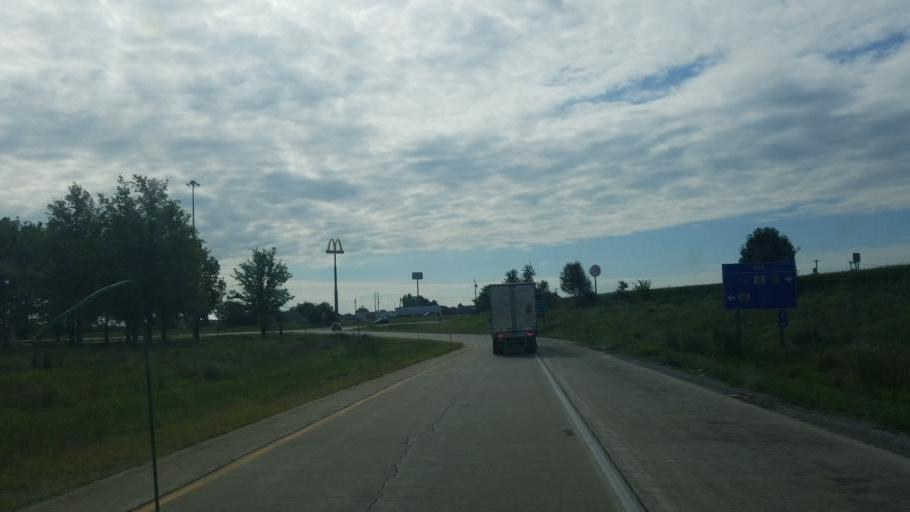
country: US
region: Illinois
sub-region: Clark County
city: Marshall
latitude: 39.4201
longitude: -87.6955
